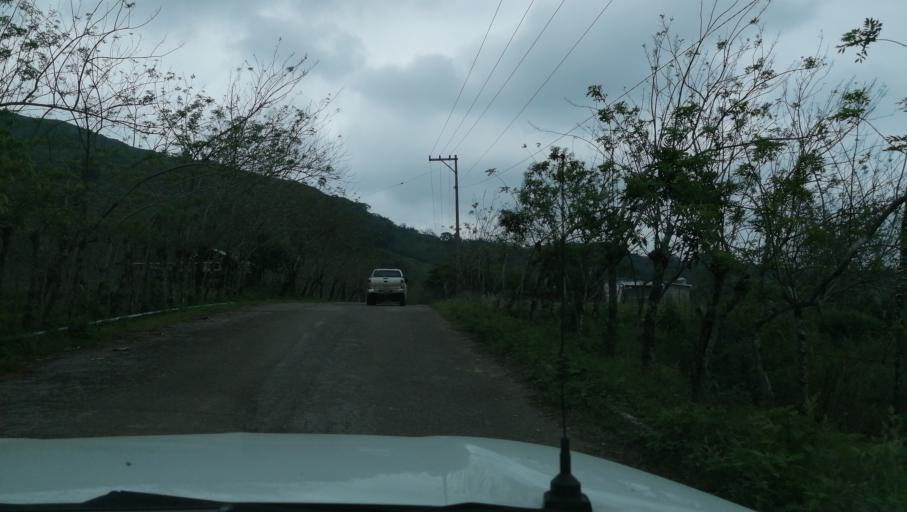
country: MX
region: Chiapas
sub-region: Francisco Leon
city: San Miguel la Sardina
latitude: 17.2777
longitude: -93.2720
